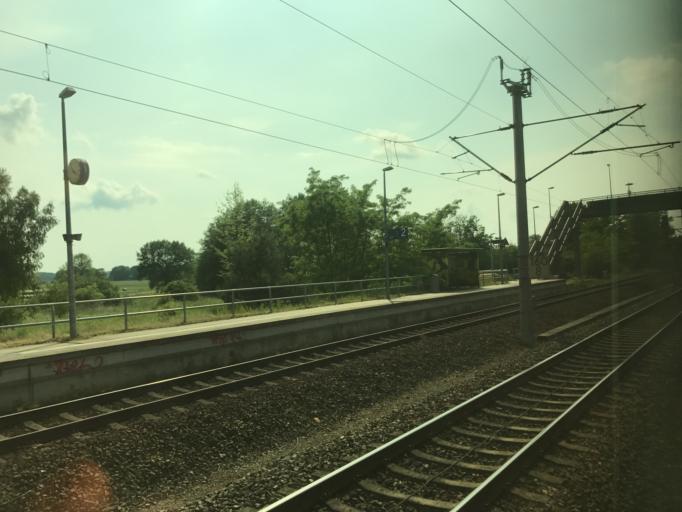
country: DE
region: Brandenburg
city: Nennhausen
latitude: 52.6000
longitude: 12.5036
